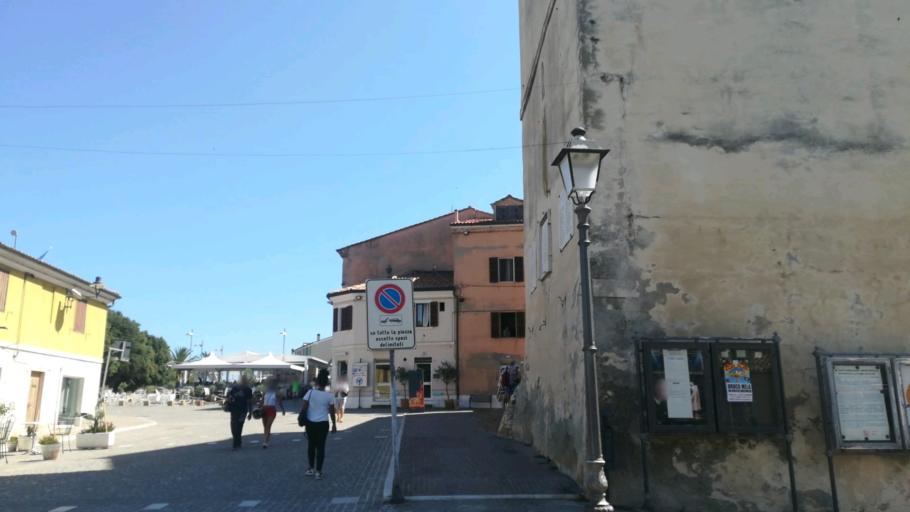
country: IT
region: The Marches
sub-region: Provincia di Ancona
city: Sirolo
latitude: 43.5233
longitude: 13.6194
